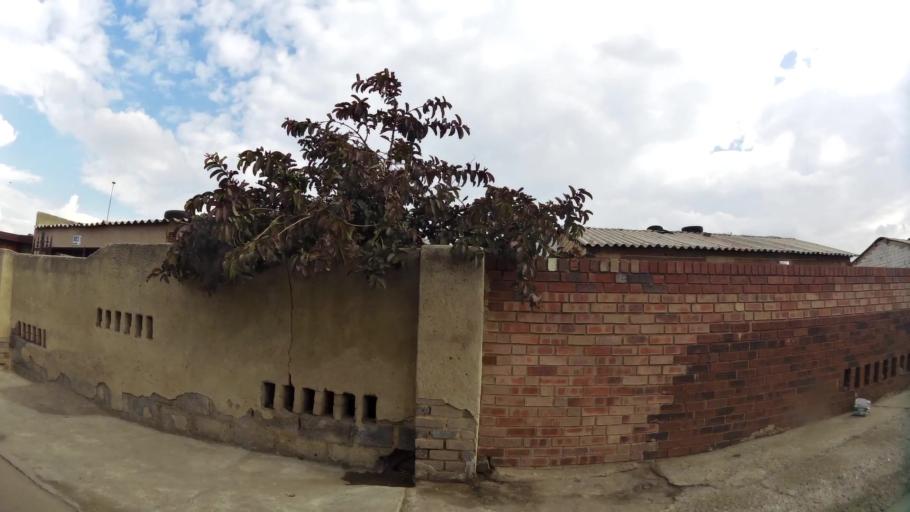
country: ZA
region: Gauteng
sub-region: City of Johannesburg Metropolitan Municipality
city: Soweto
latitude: -26.2378
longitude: 27.8636
